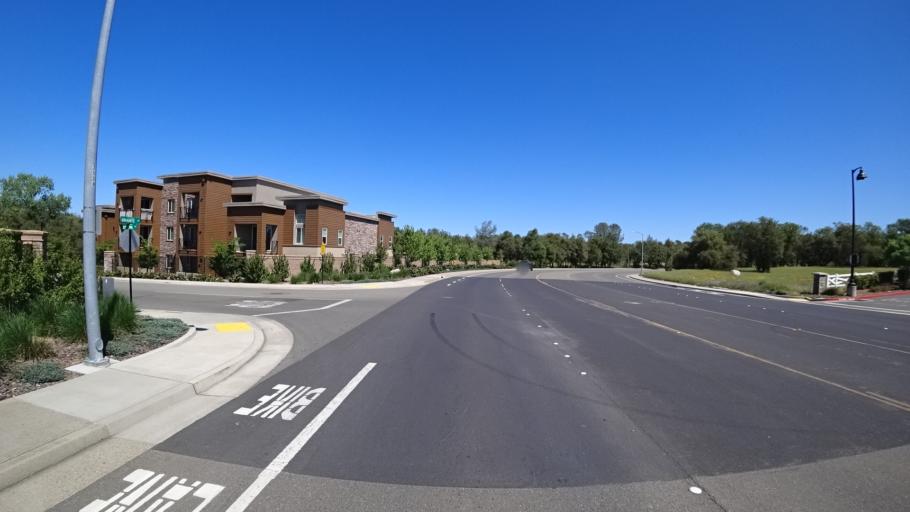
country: US
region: California
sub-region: Placer County
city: Loomis
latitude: 38.8053
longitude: -121.2103
